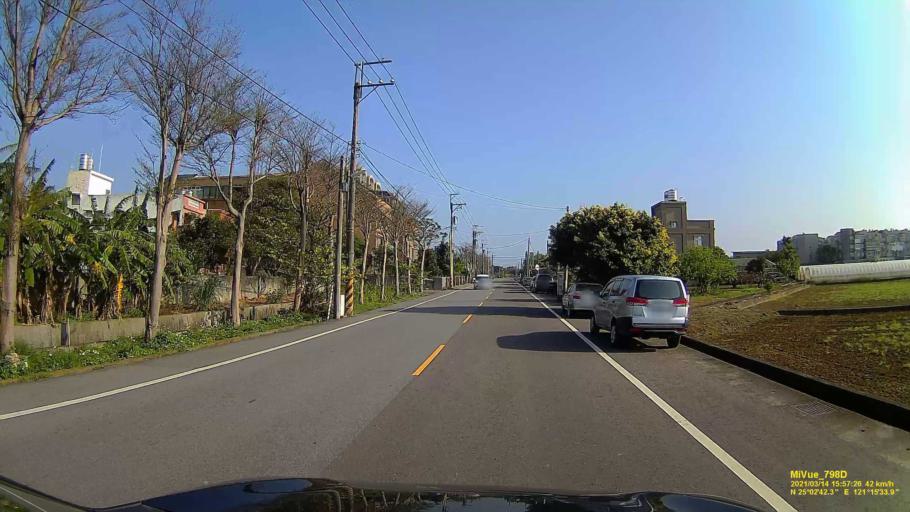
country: TW
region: Taiwan
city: Taoyuan City
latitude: 25.0450
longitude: 121.2594
